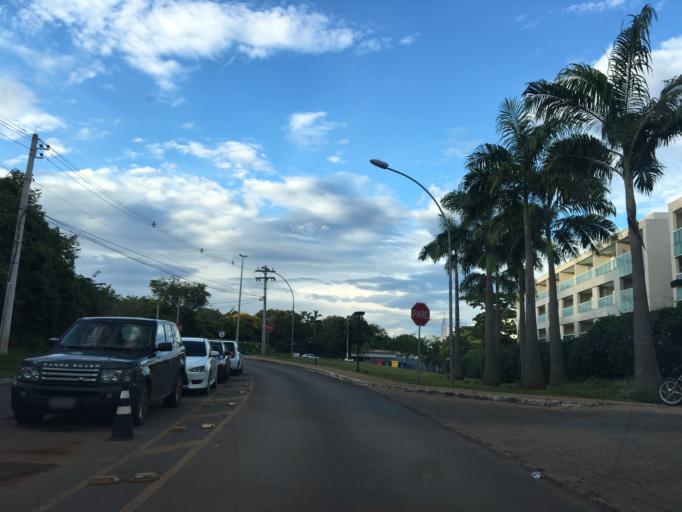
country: BR
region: Federal District
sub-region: Brasilia
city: Brasilia
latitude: -15.8069
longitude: -47.8311
